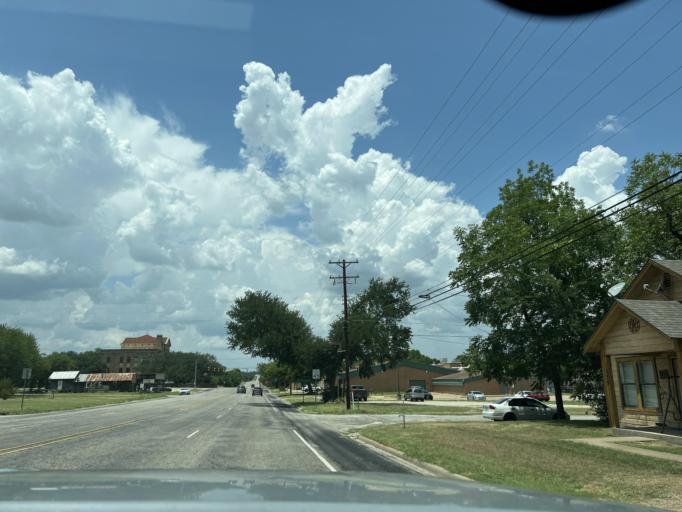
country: US
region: Texas
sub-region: Palo Pinto County
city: Palo Pinto
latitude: 32.7680
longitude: -98.2967
